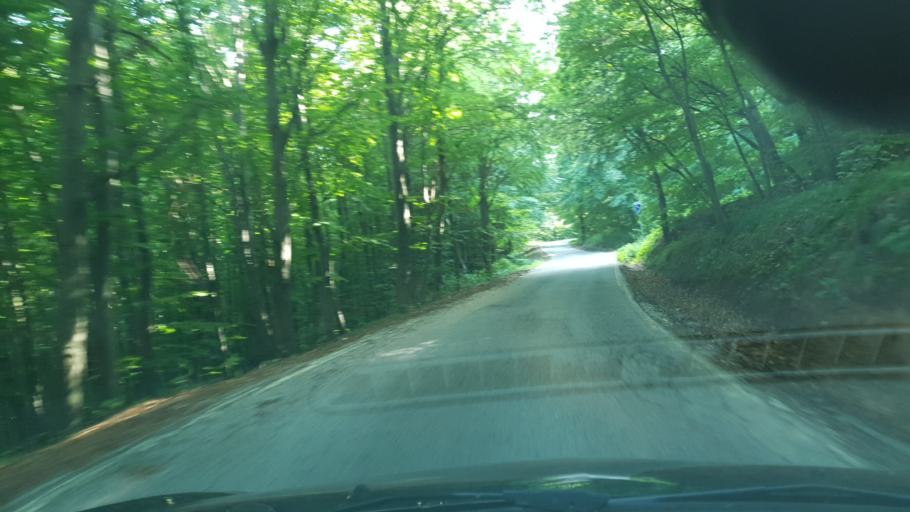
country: HR
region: Grad Zagreb
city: Kasina
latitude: 45.8842
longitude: 15.9756
